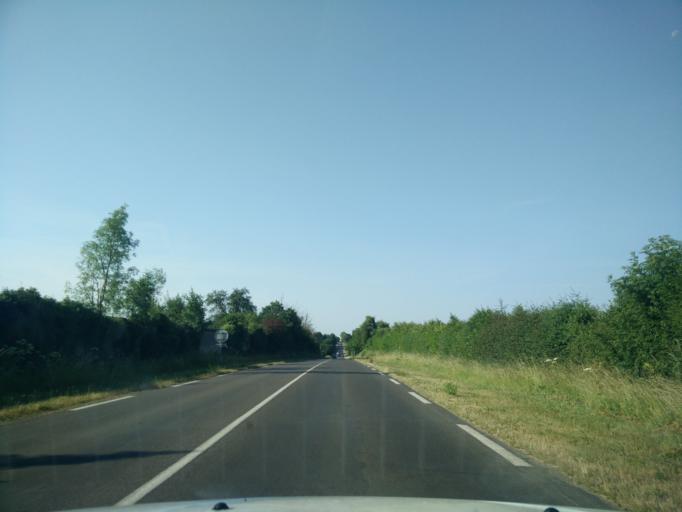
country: FR
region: Auvergne
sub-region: Departement de l'Allier
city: Toulon-sur-Allier
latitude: 46.5259
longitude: 3.3183
